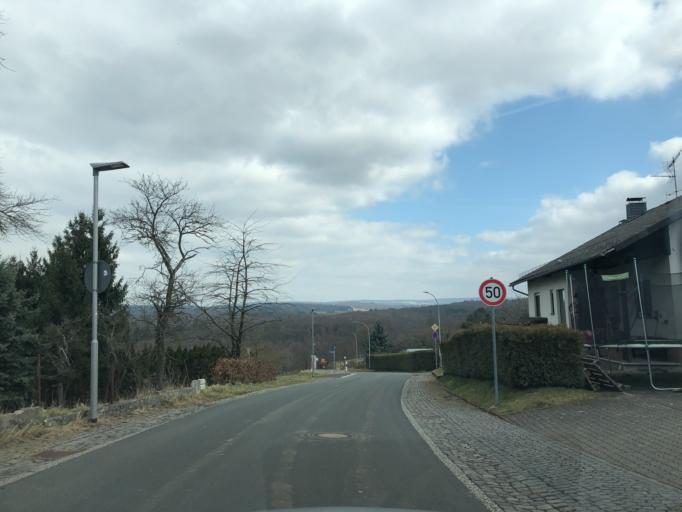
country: DE
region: Hesse
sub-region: Regierungsbezirk Giessen
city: Laubach
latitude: 50.4884
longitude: 9.0377
